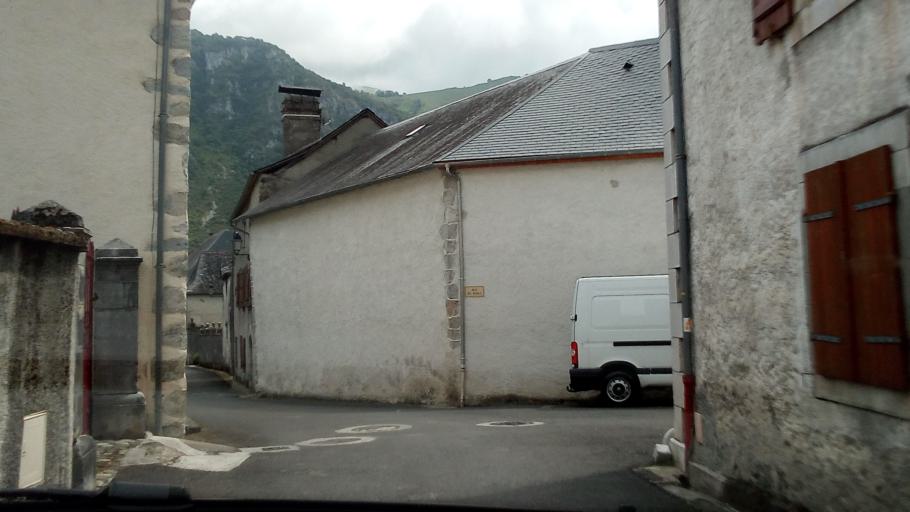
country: FR
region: Aquitaine
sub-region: Departement des Pyrenees-Atlantiques
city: Louvie-Juzon
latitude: 43.0556
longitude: -0.4341
